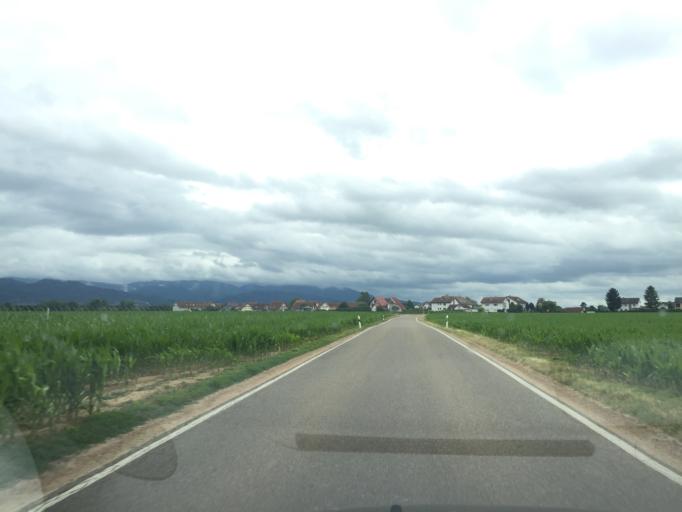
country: DE
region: Baden-Wuerttemberg
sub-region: Freiburg Region
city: Unterkrozingen
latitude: 47.9084
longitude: 7.6732
